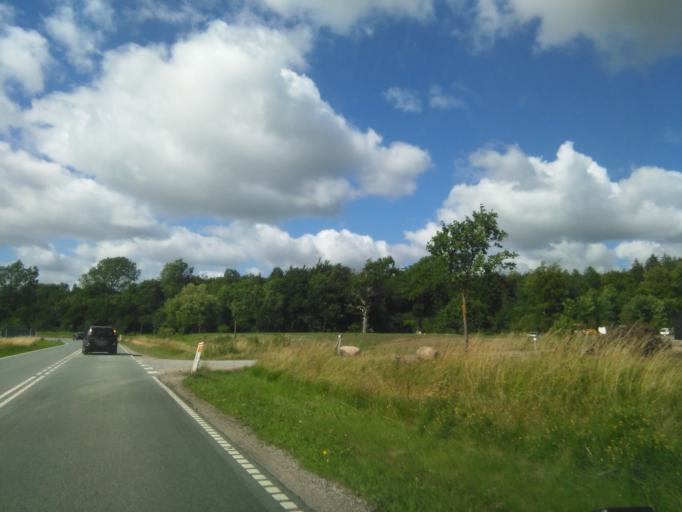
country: DK
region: Central Jutland
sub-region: Syddjurs Kommune
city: Ronde
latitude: 56.2810
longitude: 10.4871
